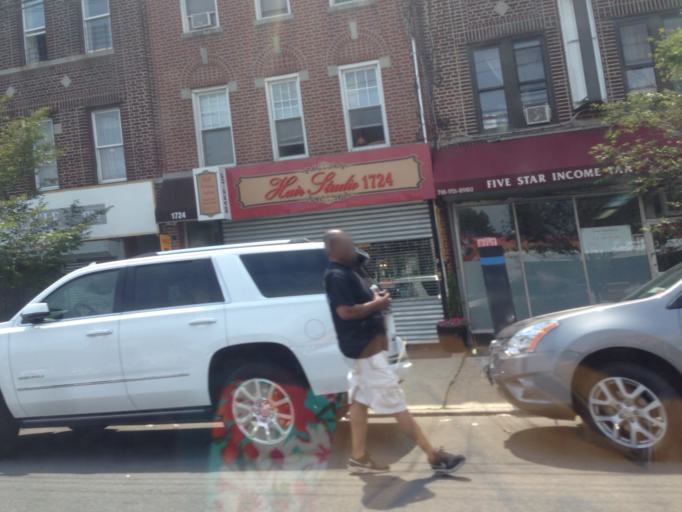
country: US
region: New York
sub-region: Kings County
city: Brooklyn
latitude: 40.6282
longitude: -73.9429
